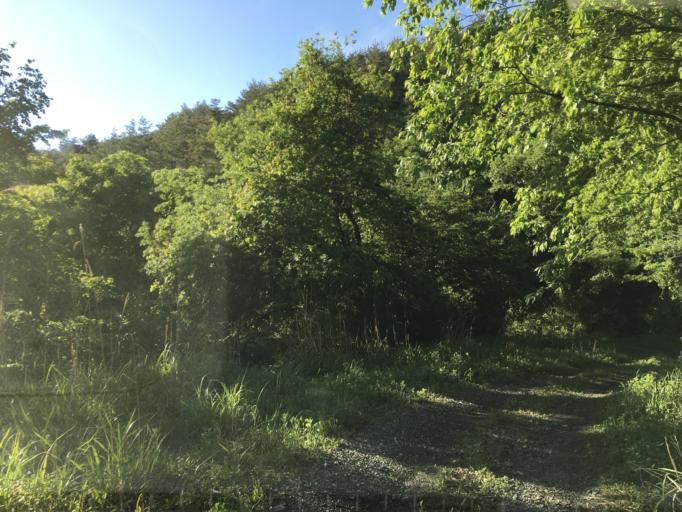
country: JP
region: Iwate
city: Ichinoseki
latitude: 38.8719
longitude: 141.4475
